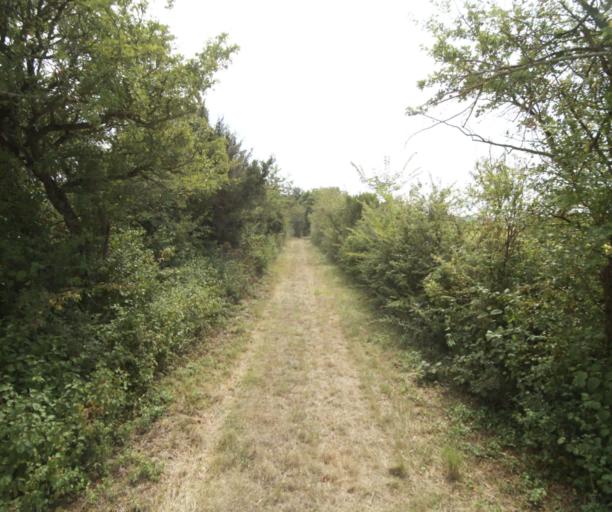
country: FR
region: Midi-Pyrenees
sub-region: Departement de la Haute-Garonne
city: Saint-Felix-Lauragais
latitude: 43.4275
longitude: 1.9235
